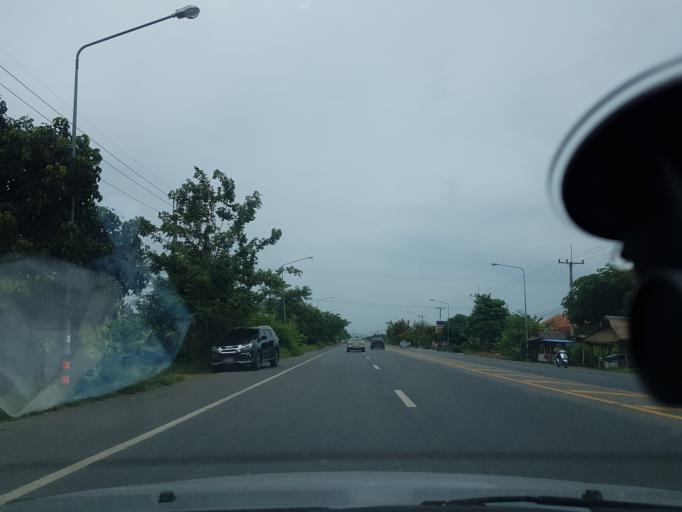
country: TH
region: Lop Buri
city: Lop Buri
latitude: 14.8091
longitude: 100.5853
